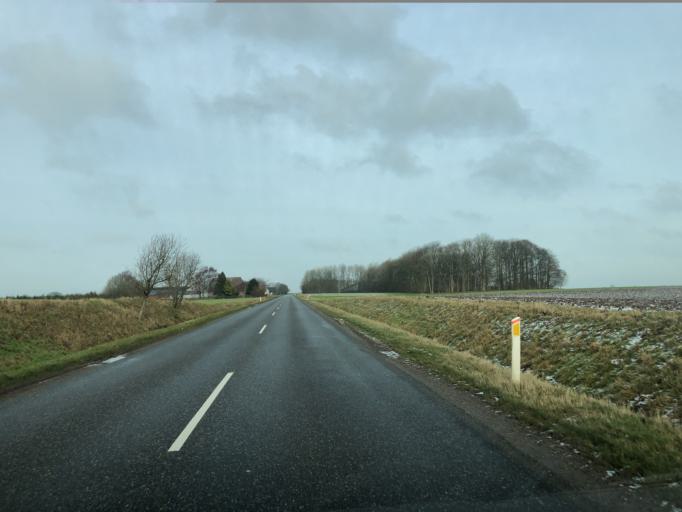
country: DK
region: South Denmark
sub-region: Vejle Kommune
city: Jelling
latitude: 55.7829
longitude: 9.4363
